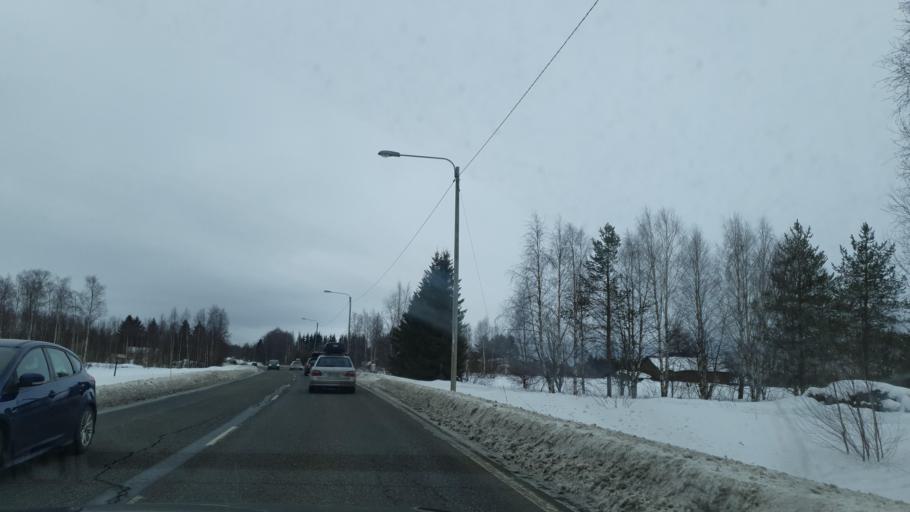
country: FI
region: Lapland
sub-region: Kemi-Tornio
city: Tornio
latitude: 66.0694
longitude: 23.9862
